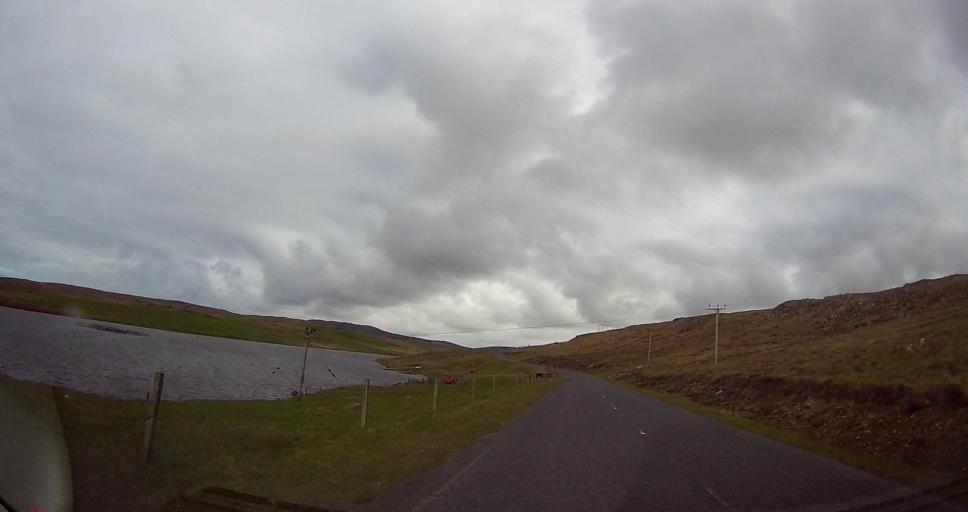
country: GB
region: Scotland
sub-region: Shetland Islands
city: Shetland
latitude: 60.6895
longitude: -0.9606
